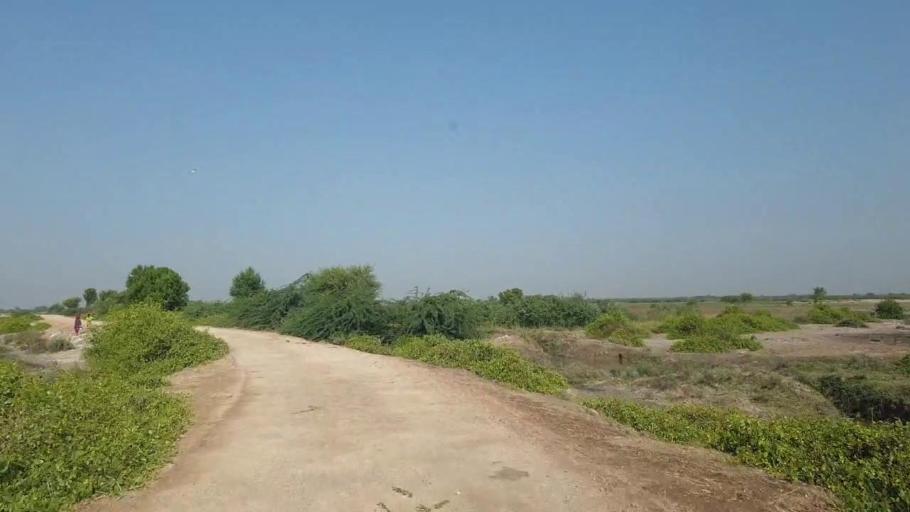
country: PK
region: Sindh
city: Badin
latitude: 24.5203
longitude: 68.7743
